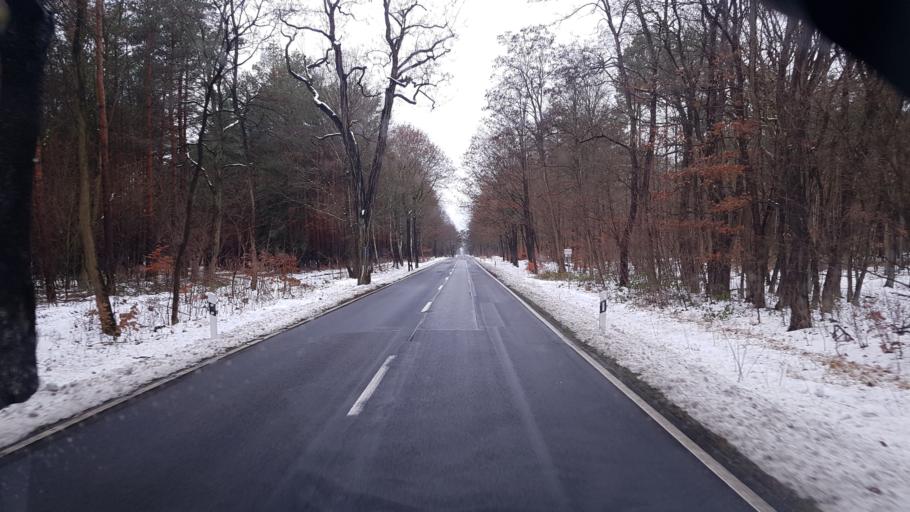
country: DE
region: Brandenburg
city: Tauer
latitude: 51.9786
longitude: 14.5053
